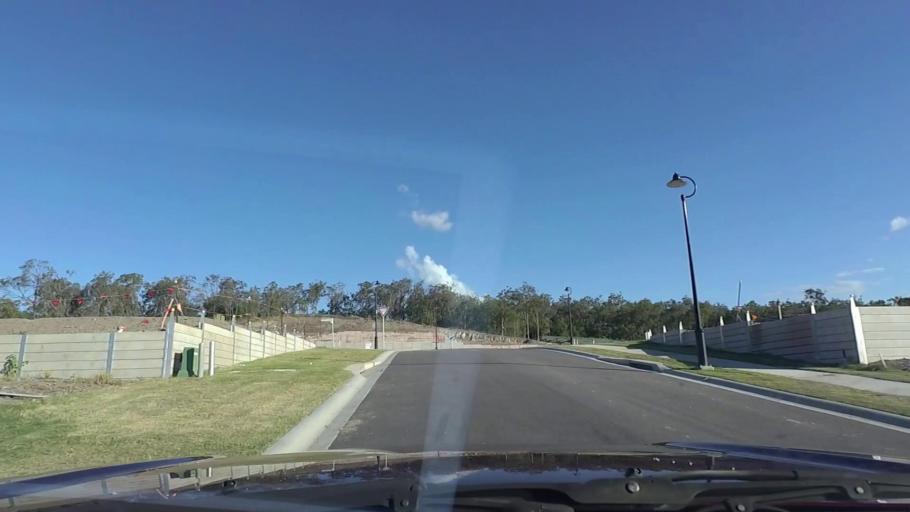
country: AU
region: Queensland
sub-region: Logan
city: Windaroo
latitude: -27.7229
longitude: 153.1695
